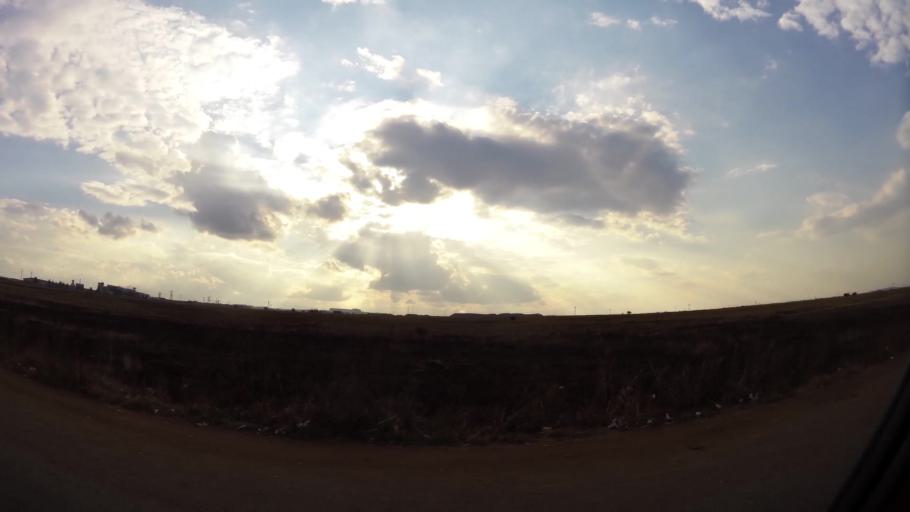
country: ZA
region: Gauteng
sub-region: Sedibeng District Municipality
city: Vereeniging
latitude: -26.6586
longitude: 27.8685
